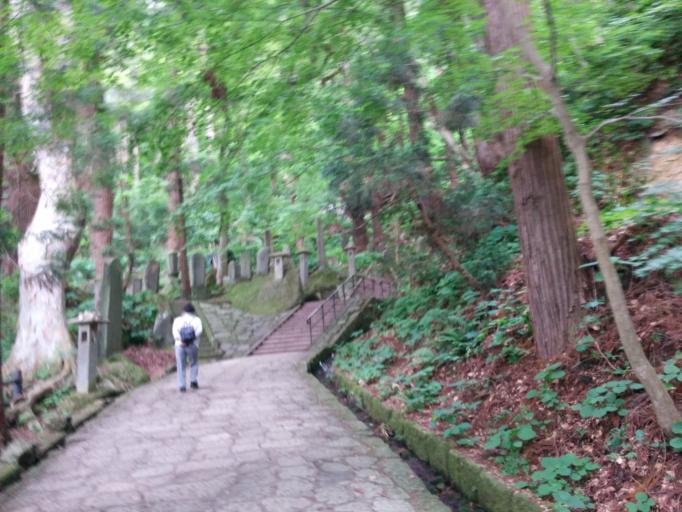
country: JP
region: Yamagata
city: Tendo
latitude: 38.3124
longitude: 140.4357
